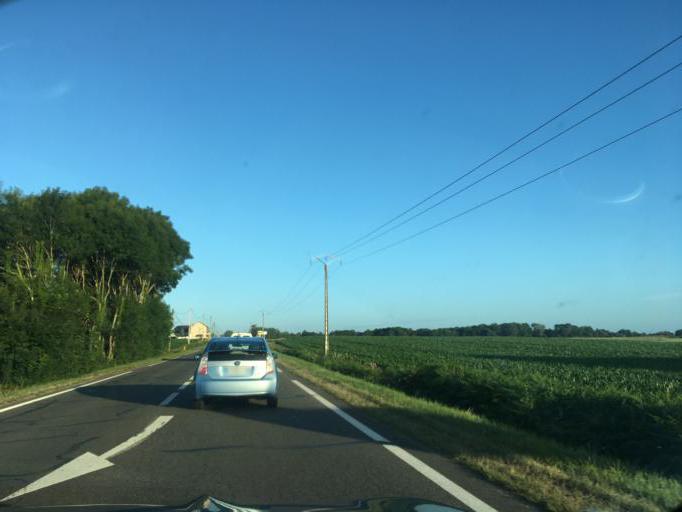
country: FR
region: Aquitaine
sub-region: Departement des Pyrenees-Atlantiques
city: Ger
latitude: 43.2449
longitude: -0.0257
